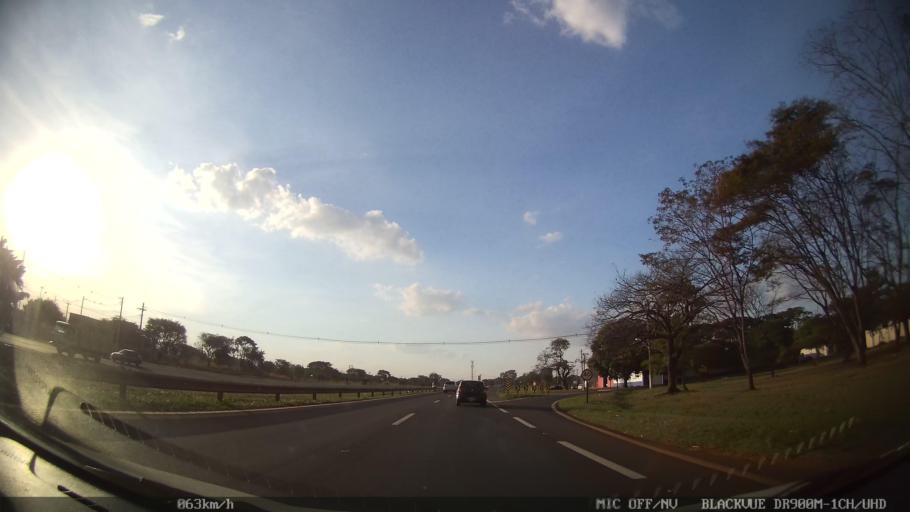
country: BR
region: Sao Paulo
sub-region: Ribeirao Preto
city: Ribeirao Preto
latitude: -21.1217
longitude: -47.7861
